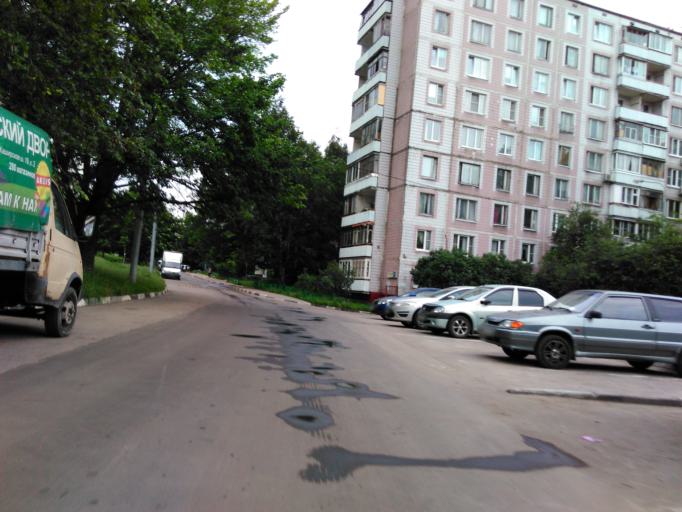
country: RU
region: Moscow
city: Yasenevo
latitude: 55.6044
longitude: 37.5455
